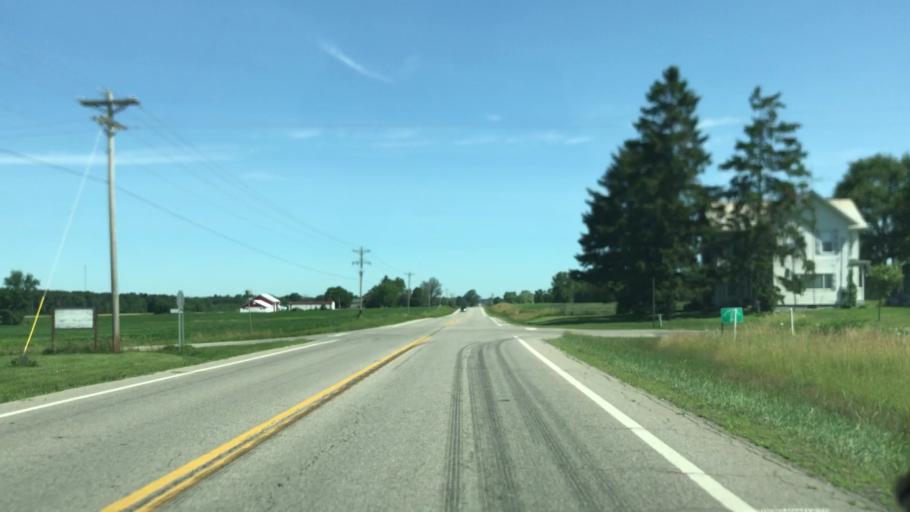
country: US
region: Ohio
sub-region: Huron County
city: Greenwich
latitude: 41.0104
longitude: -82.4844
